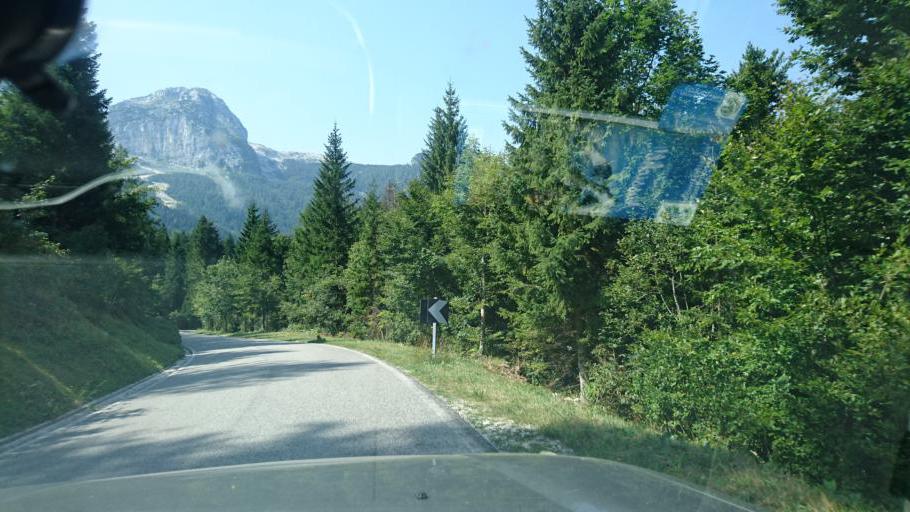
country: SI
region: Bovec
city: Bovec
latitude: 46.3905
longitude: 13.4830
